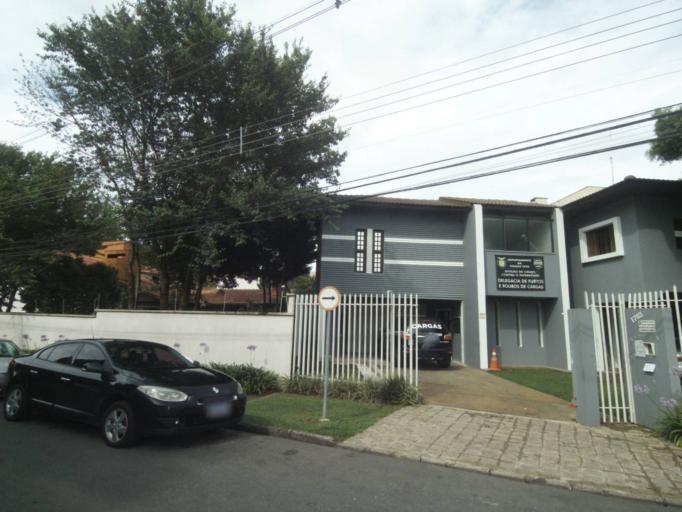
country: BR
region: Parana
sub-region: Curitiba
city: Curitiba
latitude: -25.4421
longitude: -49.3016
